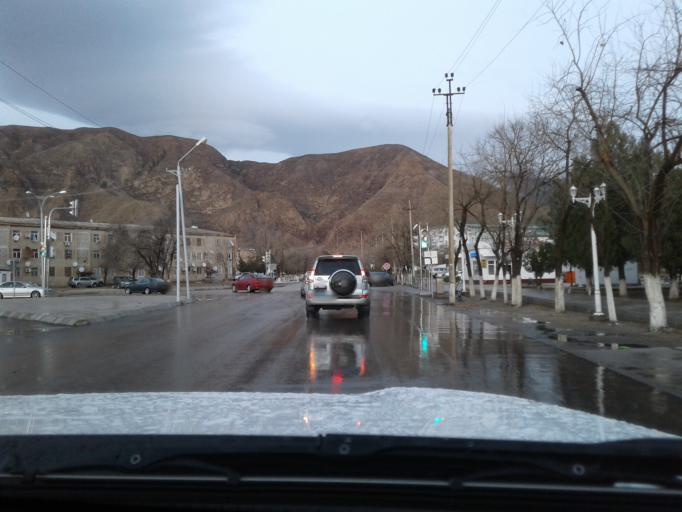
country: TM
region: Balkan
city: Balkanabat
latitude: 39.5178
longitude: 54.3633
